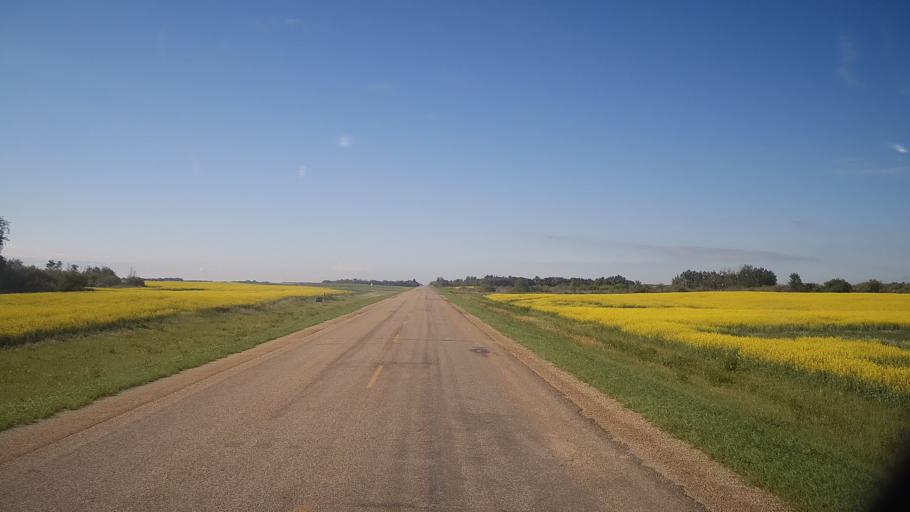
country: CA
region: Saskatchewan
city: Watrous
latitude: 51.8124
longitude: -105.2867
